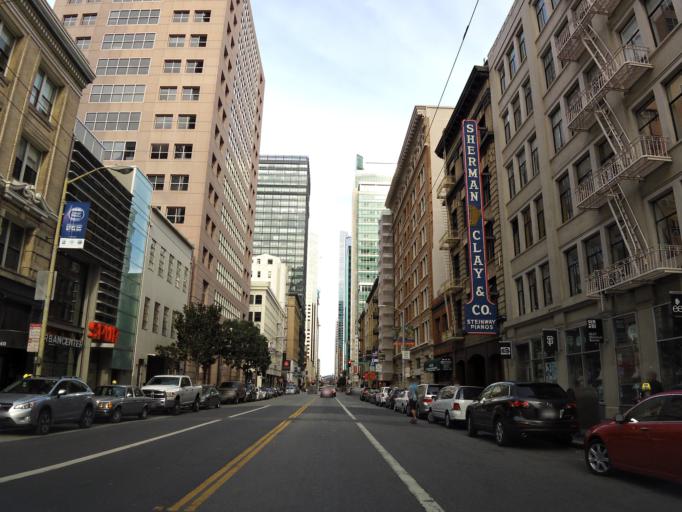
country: US
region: California
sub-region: San Francisco County
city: San Francisco
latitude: 37.7868
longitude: -122.4013
